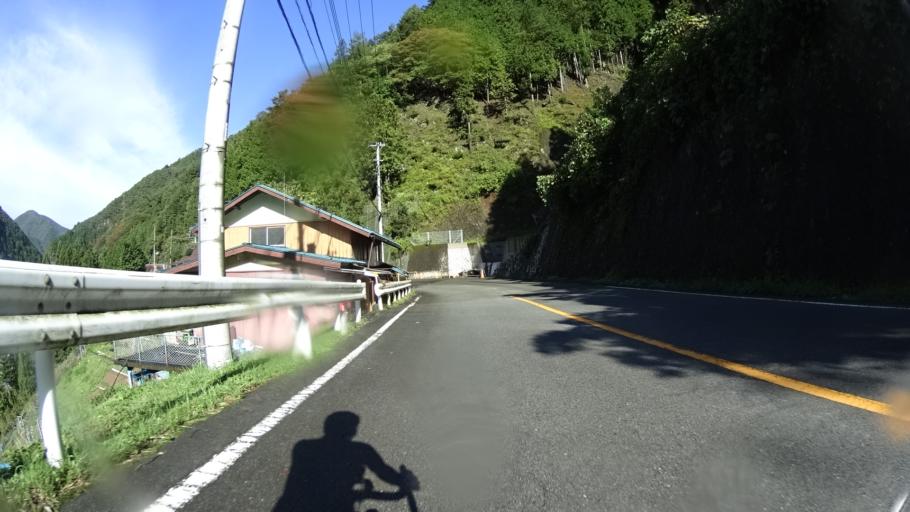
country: JP
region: Yamanashi
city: Otsuki
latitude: 35.7881
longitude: 138.9448
